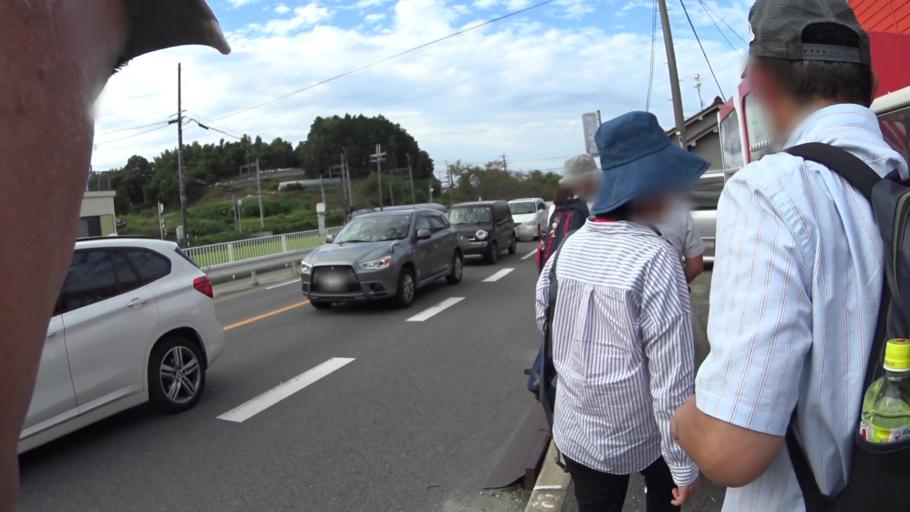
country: JP
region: Nara
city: Kashihara-shi
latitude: 34.4656
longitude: 135.7992
